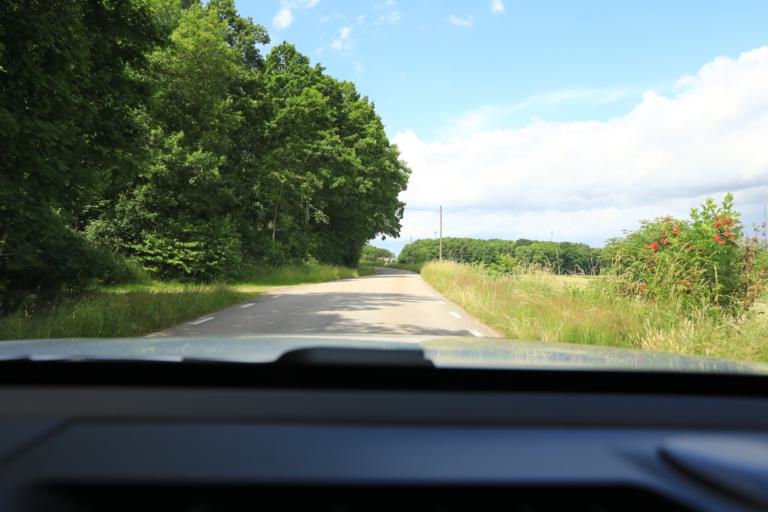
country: SE
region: Halland
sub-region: Varbergs Kommun
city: Tvaaker
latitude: 57.0923
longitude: 12.4068
